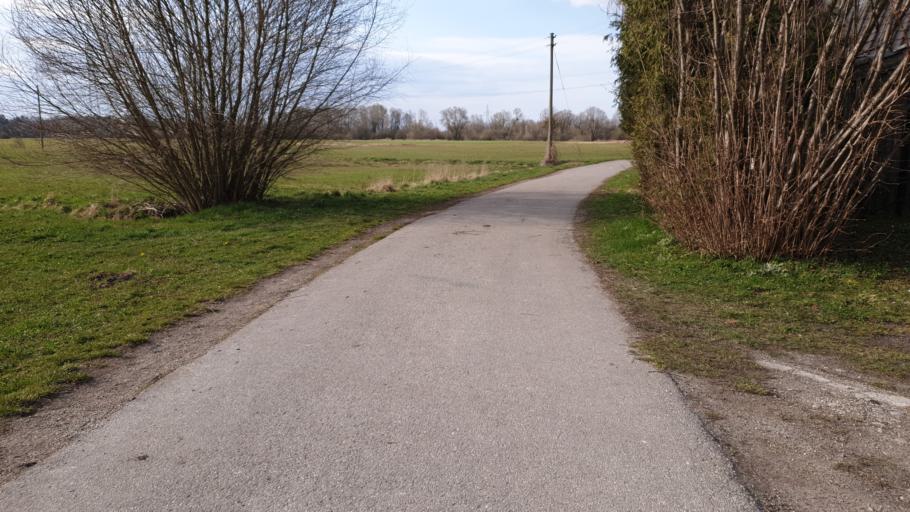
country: DE
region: Bavaria
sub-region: Upper Bavaria
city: Grobenzell
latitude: 48.1692
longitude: 11.3799
